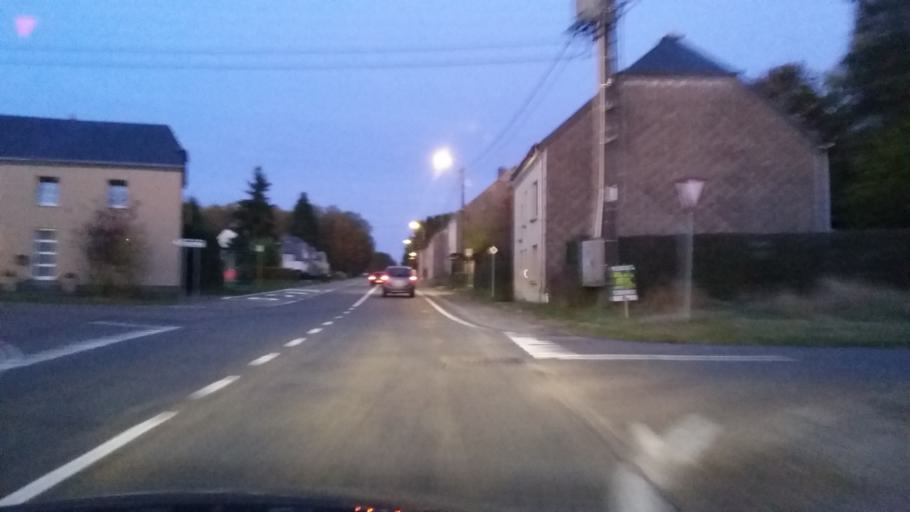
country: BE
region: Wallonia
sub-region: Province du Luxembourg
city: Saint-Leger
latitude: 49.6827
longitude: 5.7129
